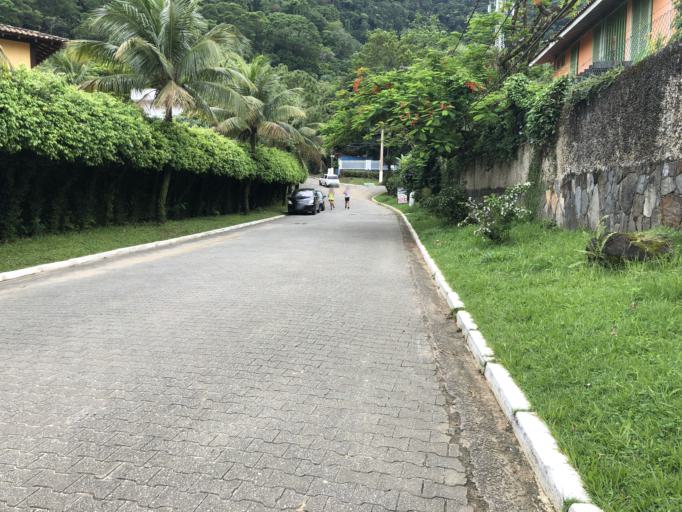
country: BR
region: Sao Paulo
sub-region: Sao Sebastiao
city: Sao Sebastiao
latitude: -23.8148
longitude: -45.5314
